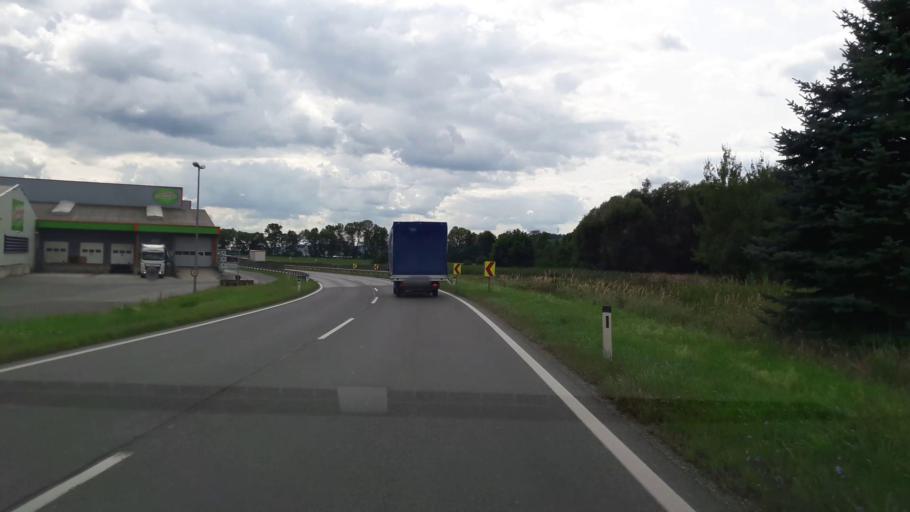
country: AT
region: Styria
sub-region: Politischer Bezirk Weiz
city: Sankt Ruprecht an der Raab
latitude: 47.1371
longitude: 15.6799
